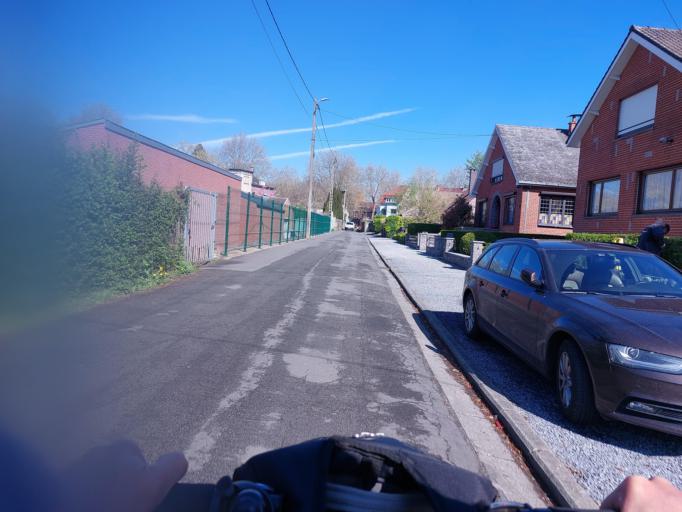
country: BE
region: Wallonia
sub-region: Province du Hainaut
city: Mons
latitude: 50.4518
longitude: 3.9680
